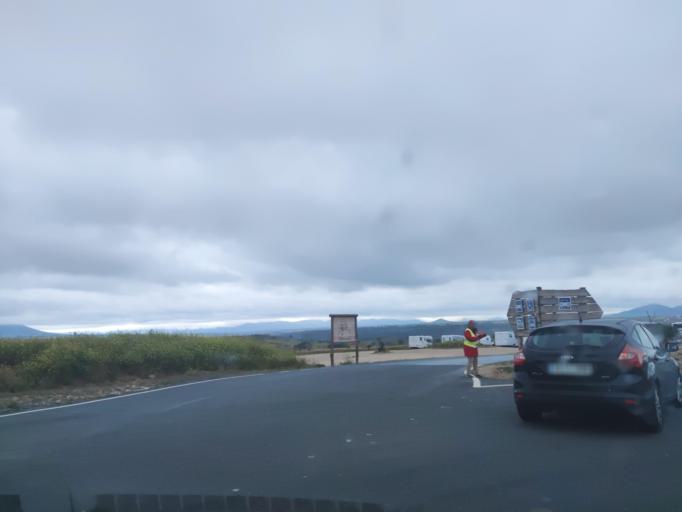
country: ES
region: Castille-La Mancha
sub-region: Province of Toledo
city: Toledo
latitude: 39.8401
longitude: -4.0841
